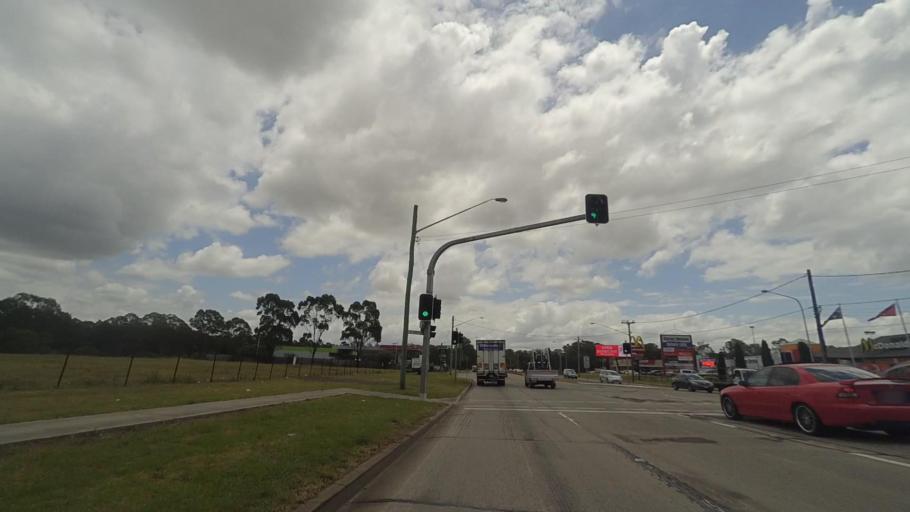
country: AU
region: New South Wales
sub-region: Fairfield
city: Cabramatta West
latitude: -33.9081
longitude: 150.9186
